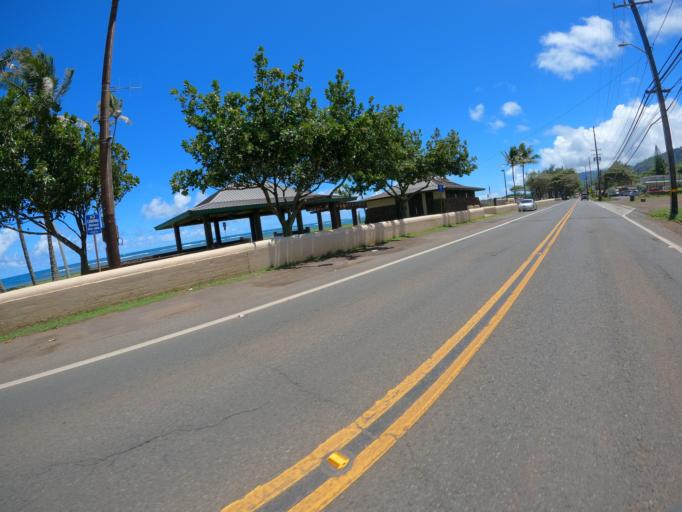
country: US
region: Hawaii
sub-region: Honolulu County
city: Hau'ula
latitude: 21.6127
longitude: -157.9117
